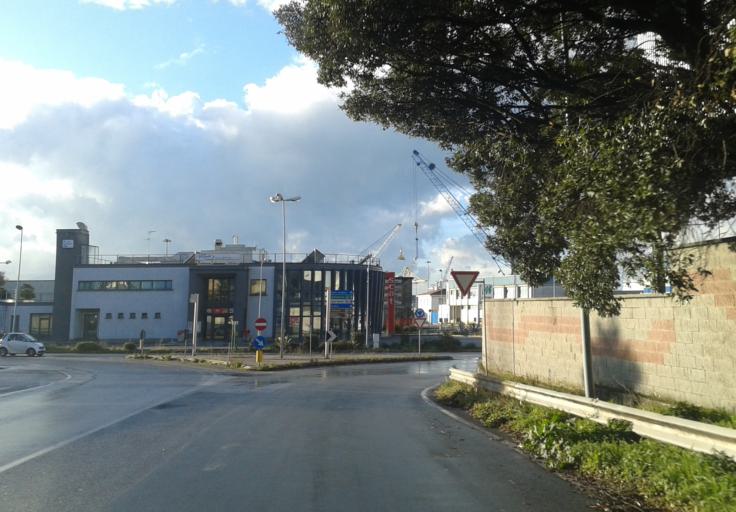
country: IT
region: Tuscany
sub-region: Provincia di Livorno
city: Livorno
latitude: 43.5713
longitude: 10.3174
